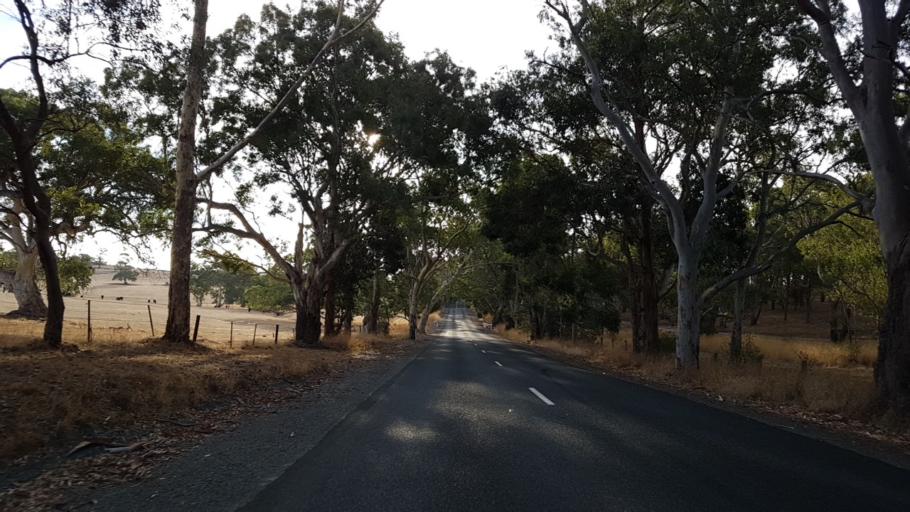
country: AU
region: South Australia
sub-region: Adelaide Hills
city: Woodside
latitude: -34.9795
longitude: 138.8882
